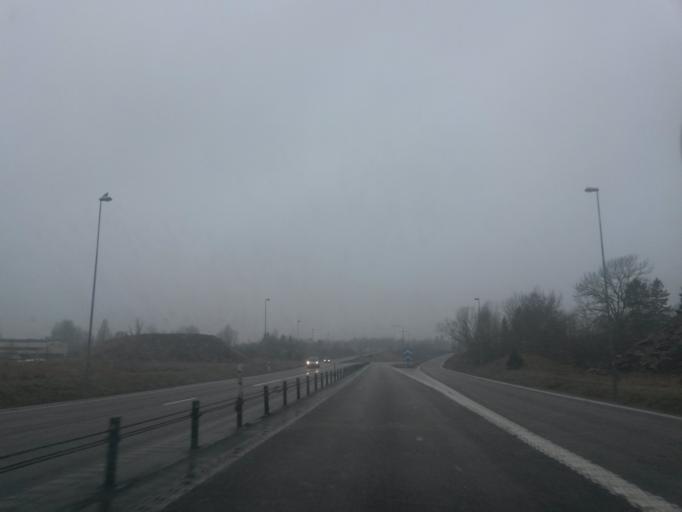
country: SE
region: Vaestra Goetaland
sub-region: Trollhattan
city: Trollhattan
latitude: 58.2988
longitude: 12.3391
